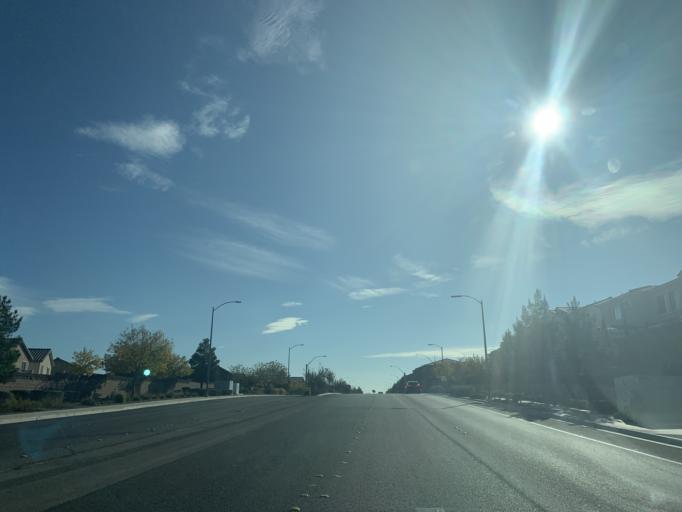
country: US
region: Nevada
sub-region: Clark County
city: Summerlin South
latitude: 36.3083
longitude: -115.3059
